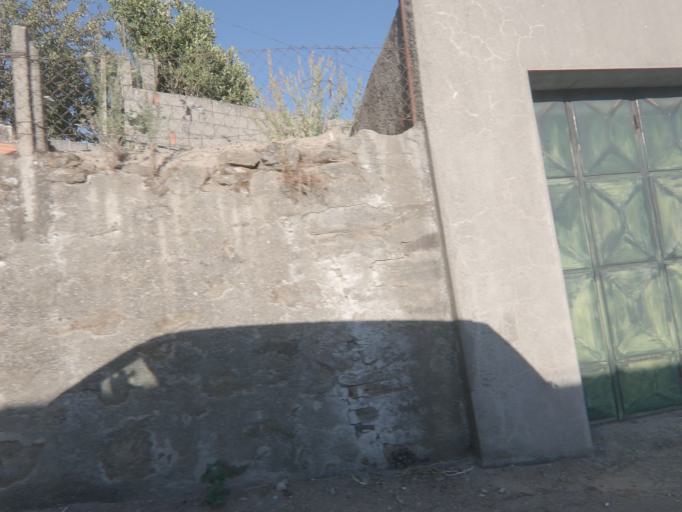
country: PT
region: Vila Real
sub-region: Peso da Regua
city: Godim
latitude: 41.1584
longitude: -7.8154
